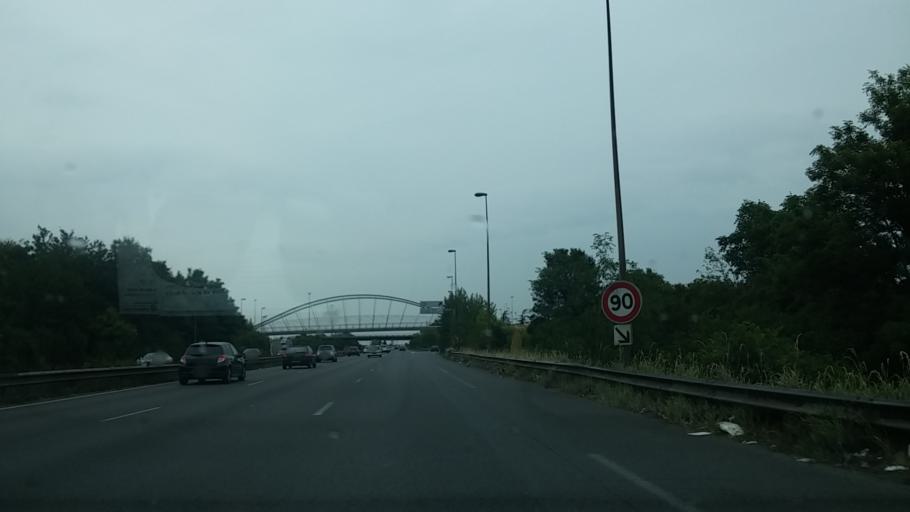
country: FR
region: Ile-de-France
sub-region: Departement de Seine-Saint-Denis
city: Villepinte
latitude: 48.9627
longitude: 2.5484
